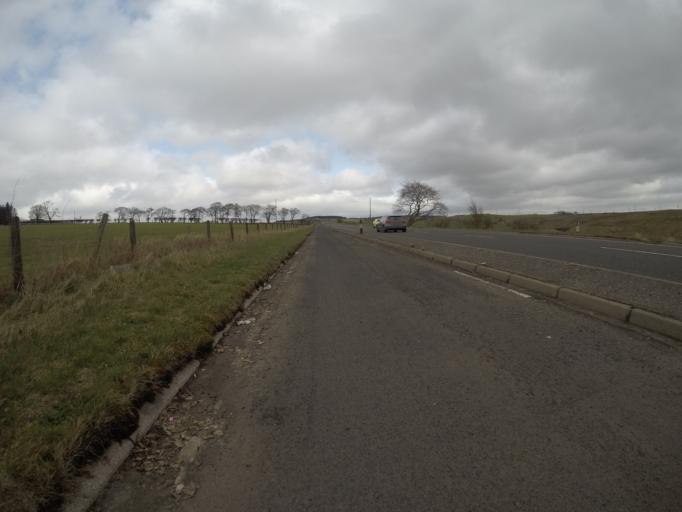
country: GB
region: Scotland
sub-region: East Ayrshire
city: Galston
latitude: 55.6865
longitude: -4.4147
